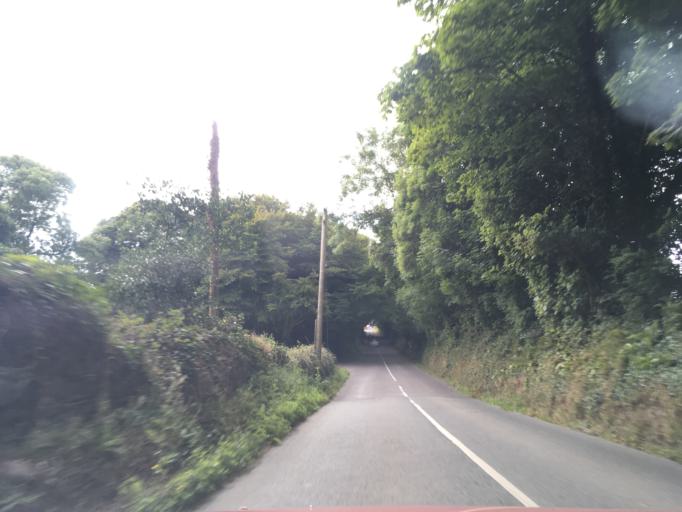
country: IE
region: Munster
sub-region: County Cork
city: Crosshaven
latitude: 51.7962
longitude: -8.2991
